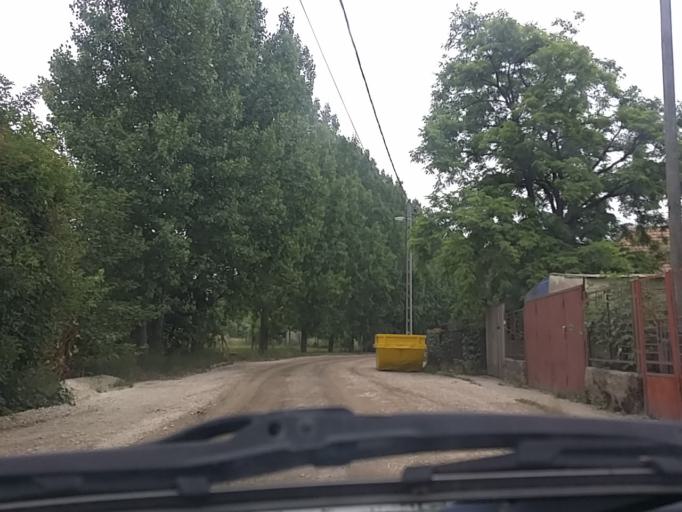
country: HU
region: Pest
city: Pilisborosjeno
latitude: 47.5980
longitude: 18.9755
